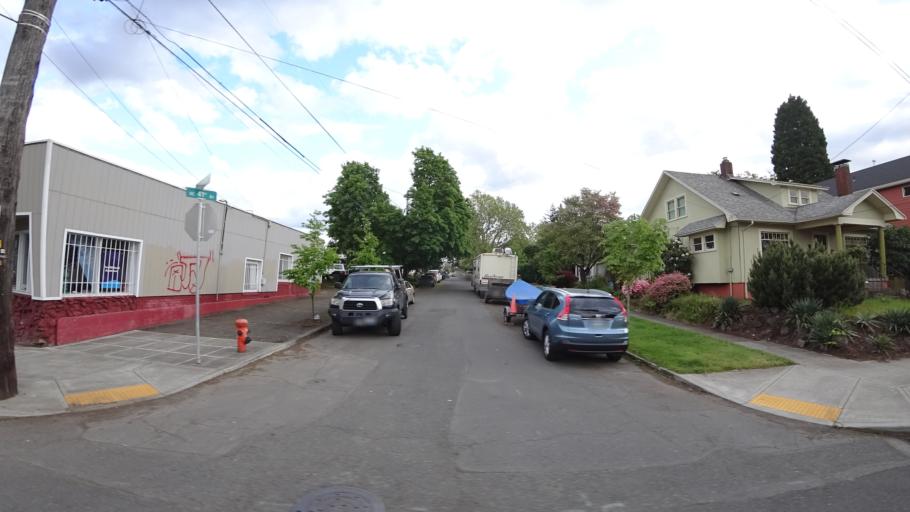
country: US
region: Oregon
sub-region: Multnomah County
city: Portland
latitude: 45.5627
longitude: -122.6216
